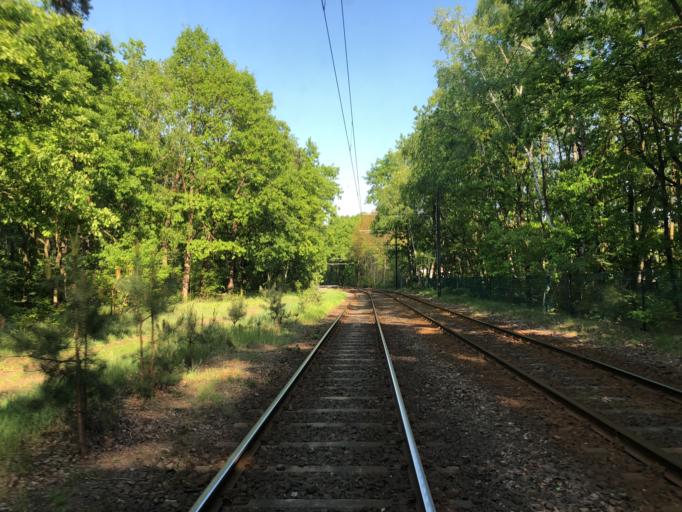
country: DE
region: Berlin
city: Grunau
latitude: 52.4107
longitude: 13.5815
